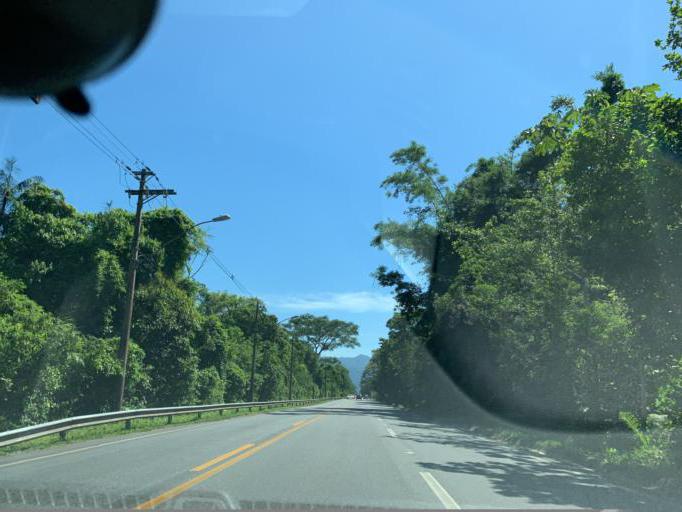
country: BR
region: Sao Paulo
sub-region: Bertioga
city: Bertioga
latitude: -23.7783
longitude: -46.0530
